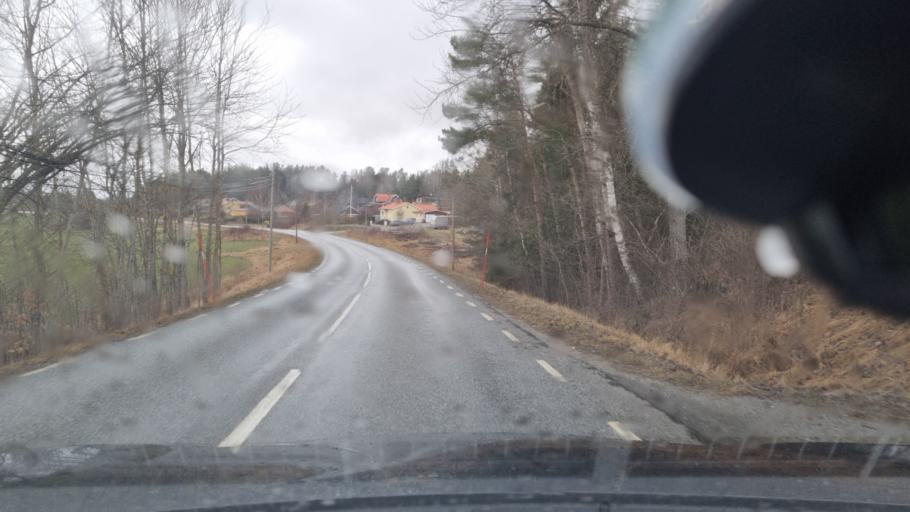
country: SE
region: Stockholm
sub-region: Sigtuna Kommun
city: Sigtuna
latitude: 59.5789
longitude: 17.6758
